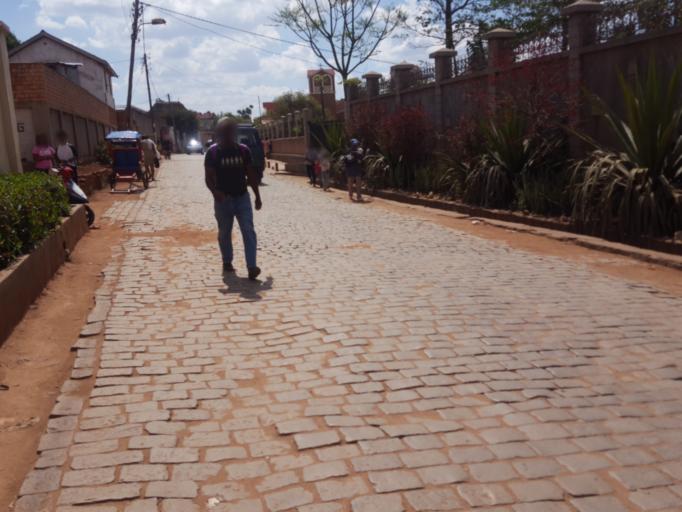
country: MG
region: Analamanga
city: Antananarivo
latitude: -18.9800
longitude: 47.5309
